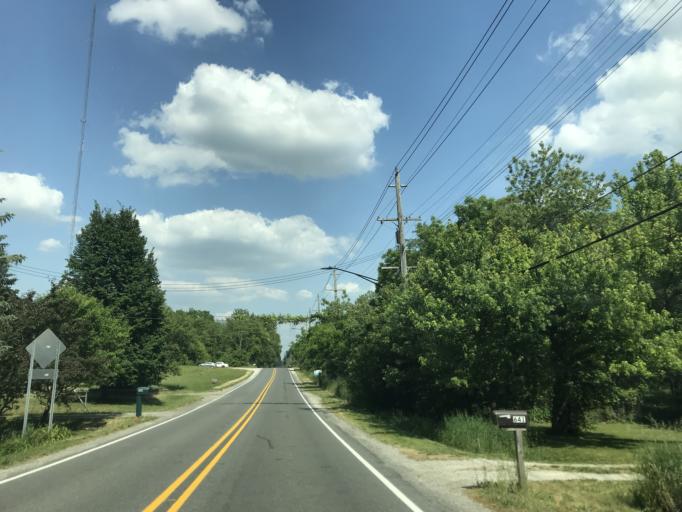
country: US
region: Michigan
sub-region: Washtenaw County
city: Ypsilanti
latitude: 42.2604
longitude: -83.6209
